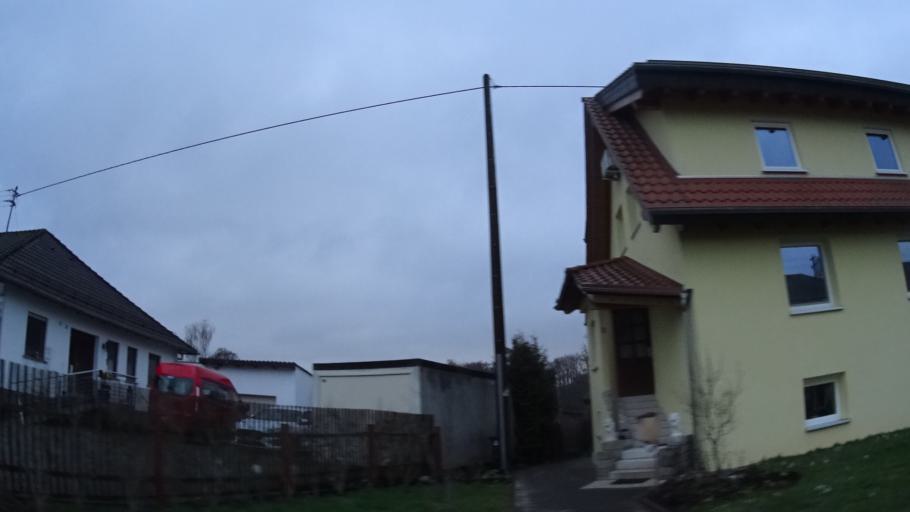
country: DE
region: Rheinland-Pfalz
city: Brucken
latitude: 49.6325
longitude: 7.1140
